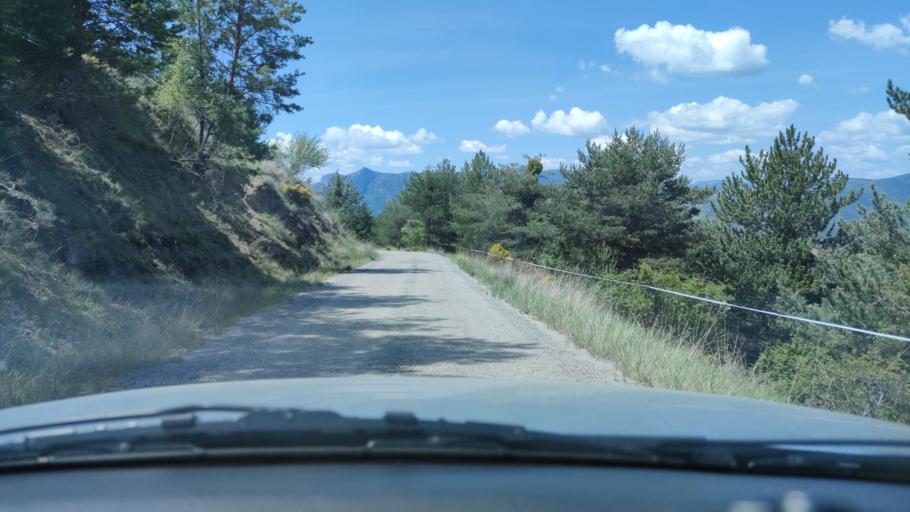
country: ES
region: Catalonia
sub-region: Provincia de Lleida
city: Sort
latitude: 42.3231
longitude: 1.0937
